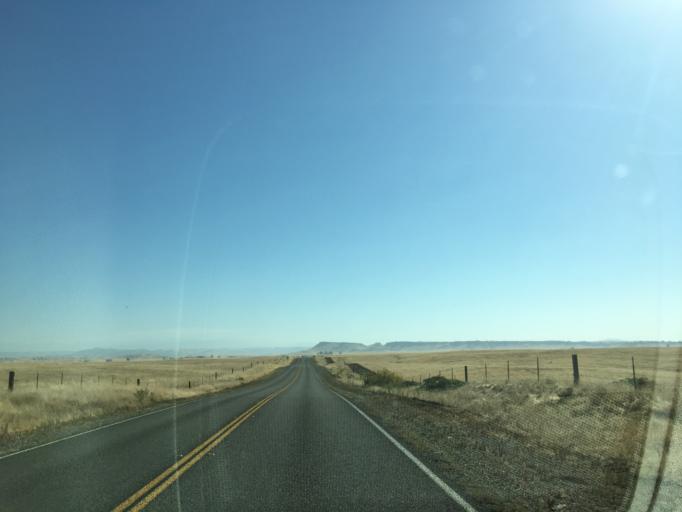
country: US
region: California
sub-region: Madera County
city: Bonadelle Ranchos-Madera Ranchos
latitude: 37.0104
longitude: -119.8343
